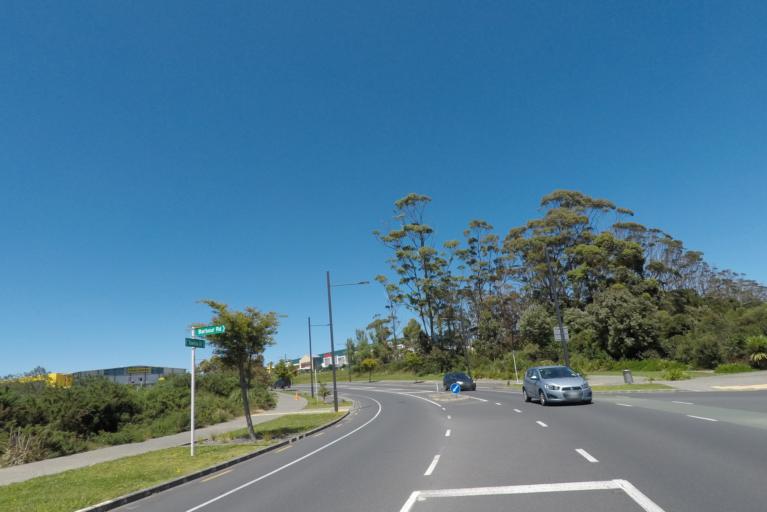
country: NZ
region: Auckland
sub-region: Auckland
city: Rosebank
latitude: -36.8174
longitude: 174.6084
